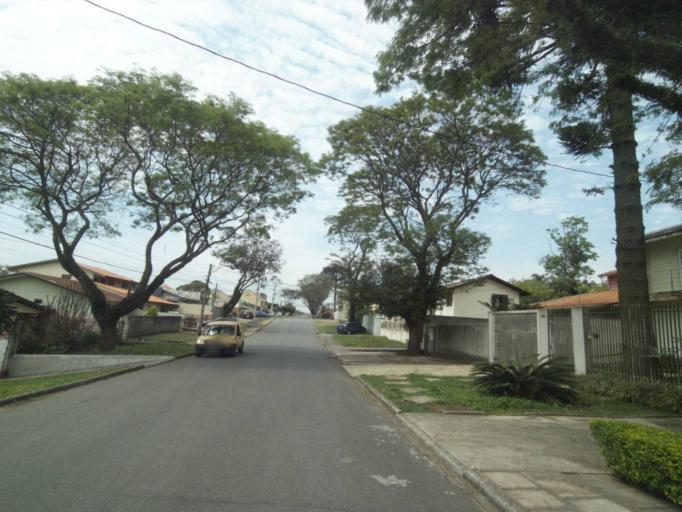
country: BR
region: Parana
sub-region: Pinhais
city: Pinhais
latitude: -25.4097
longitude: -49.2051
